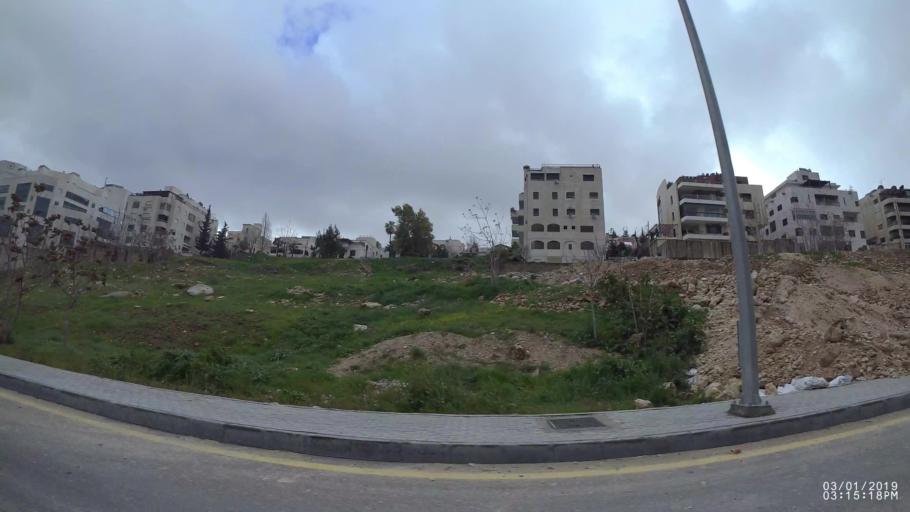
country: JO
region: Amman
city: Amman
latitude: 31.9521
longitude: 35.8923
